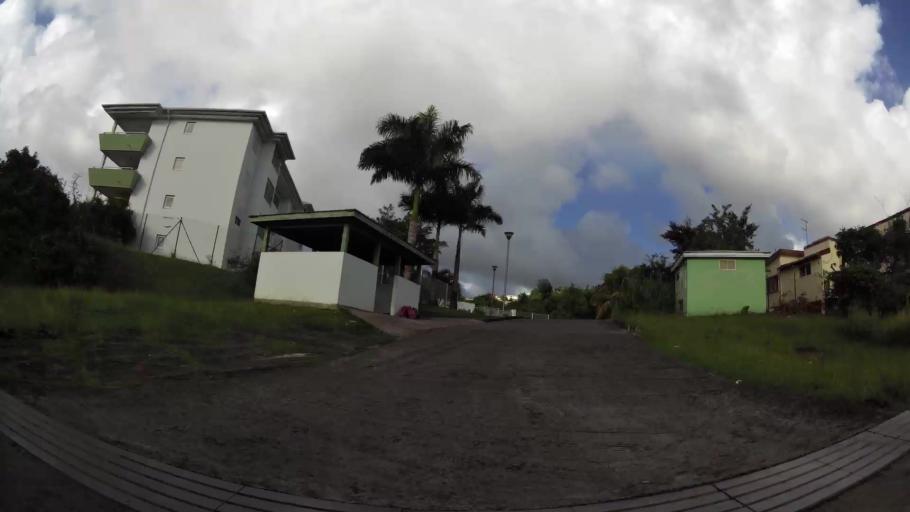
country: MQ
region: Martinique
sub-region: Martinique
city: Ducos
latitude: 14.5602
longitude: -60.9643
